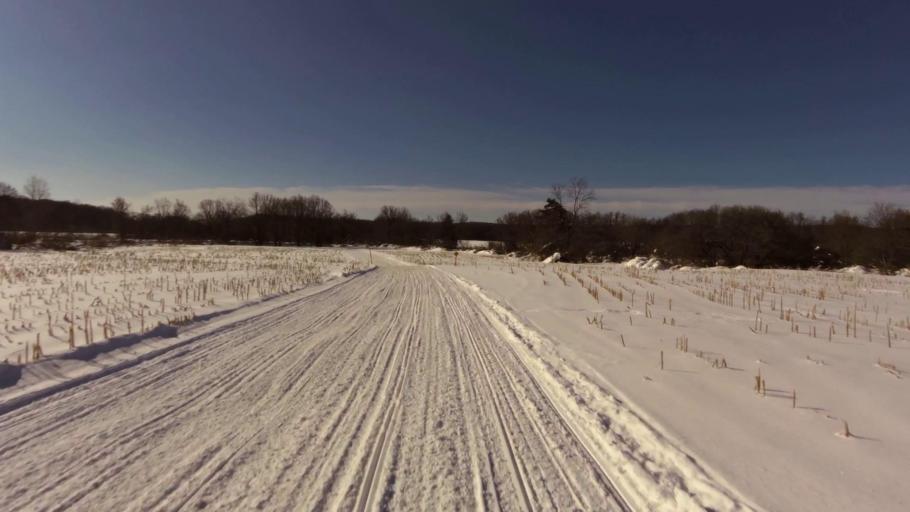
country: US
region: New York
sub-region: Cattaraugus County
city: Franklinville
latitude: 42.3973
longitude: -78.4732
